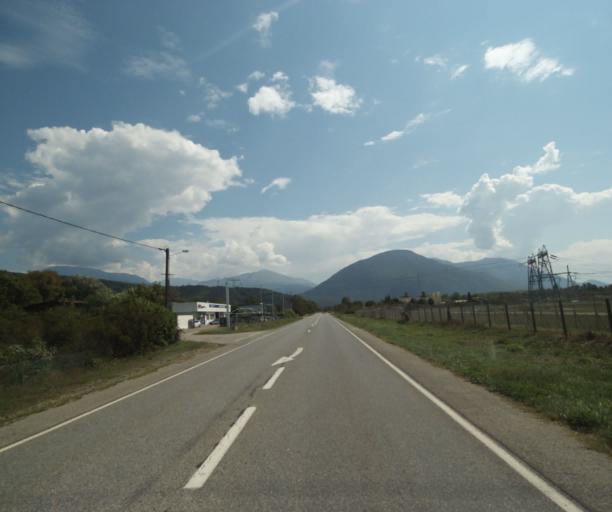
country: FR
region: Rhone-Alpes
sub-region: Departement de l'Isere
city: Champagnier
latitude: 45.1079
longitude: 5.7107
